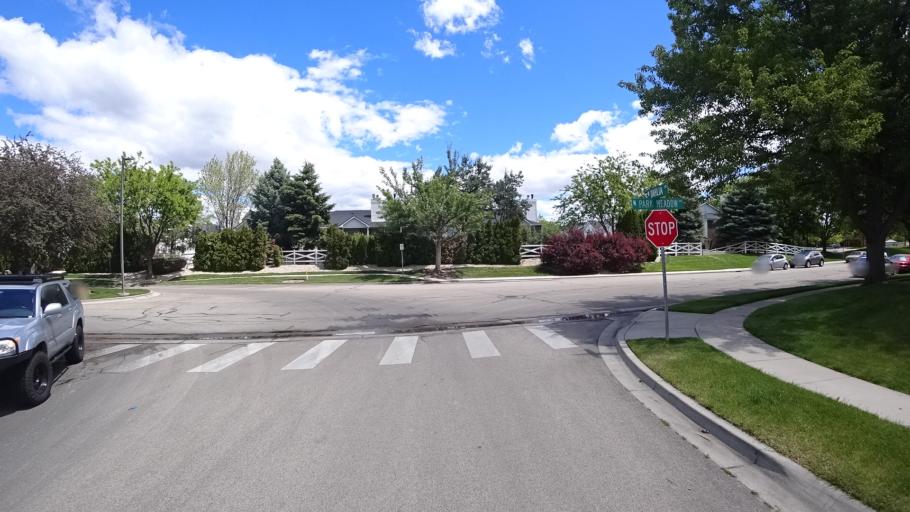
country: US
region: Idaho
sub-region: Ada County
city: Eagle
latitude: 43.6611
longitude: -116.3466
